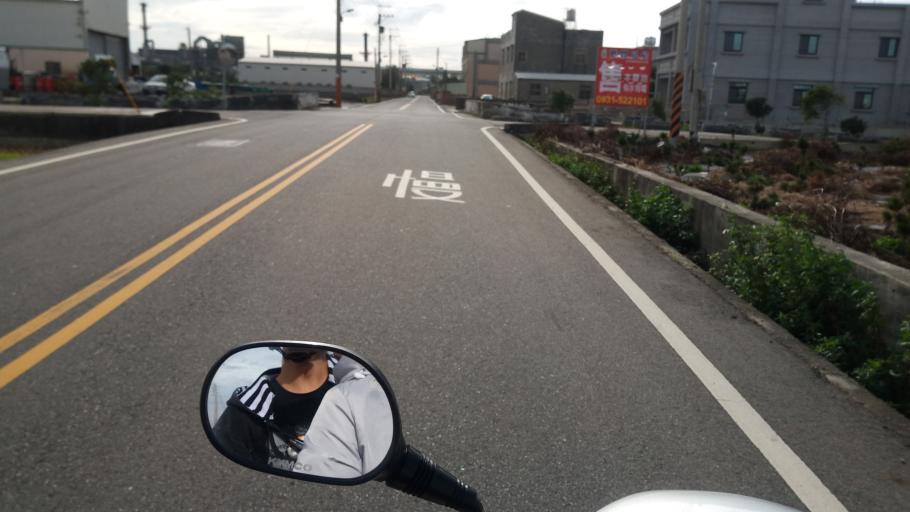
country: TW
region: Taiwan
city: Fengyuan
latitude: 24.4146
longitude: 120.6497
